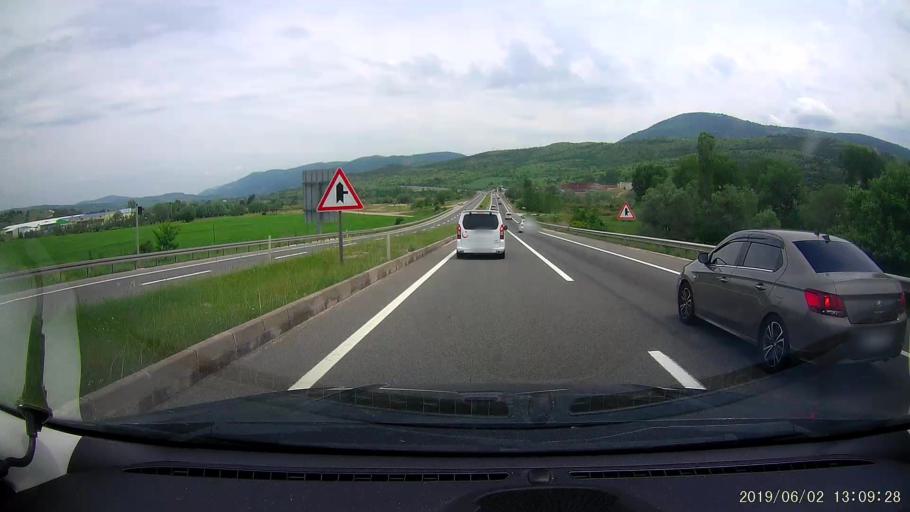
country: TR
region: Karabuk
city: Gozyeri
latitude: 40.8691
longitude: 32.5892
